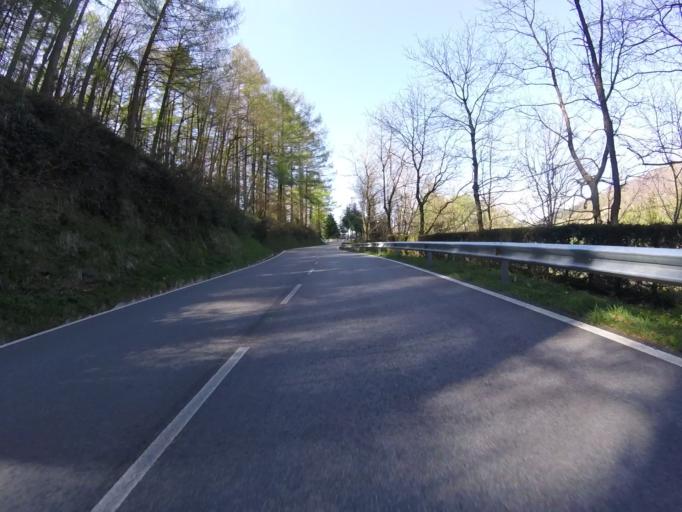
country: ES
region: Navarre
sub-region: Provincia de Navarra
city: Leitza
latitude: 43.0897
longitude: -1.8879
